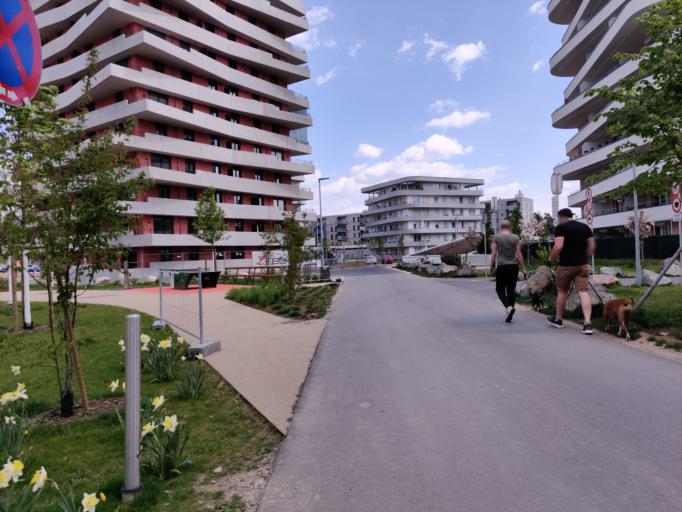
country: AT
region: Styria
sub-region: Graz Stadt
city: Wetzelsdorf
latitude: 47.0376
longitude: 15.3939
